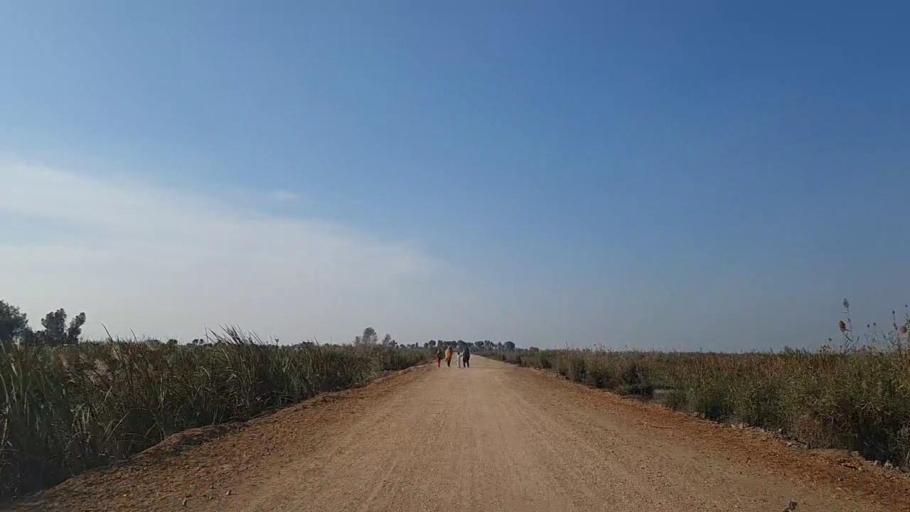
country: PK
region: Sindh
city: Bandhi
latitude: 26.6080
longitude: 68.3128
